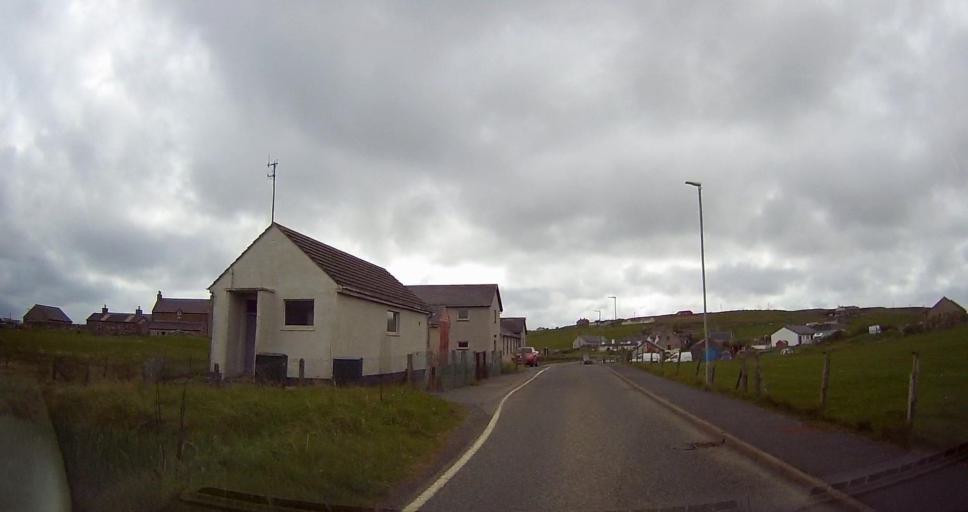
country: GB
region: Scotland
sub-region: Shetland Islands
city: Sandwick
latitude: 60.2300
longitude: -1.5620
